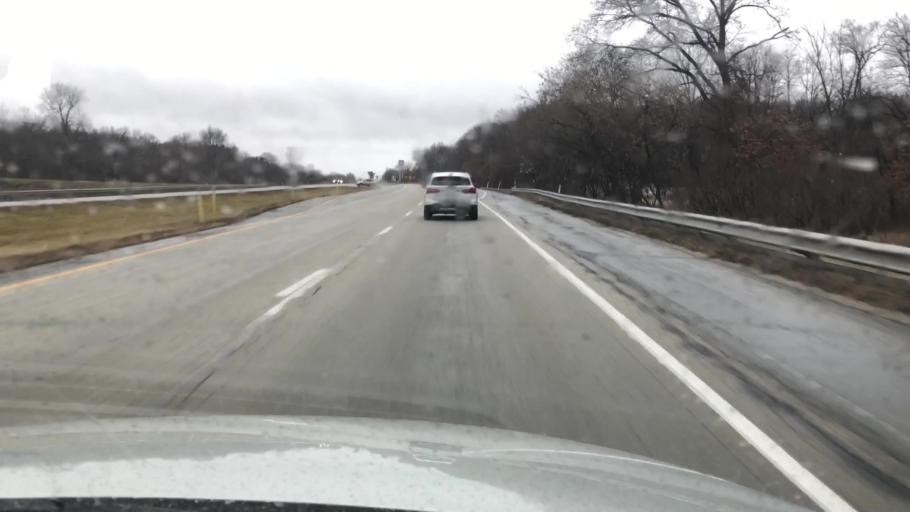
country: US
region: Indiana
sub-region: Starke County
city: Koontz Lake
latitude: 41.3681
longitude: -86.4838
